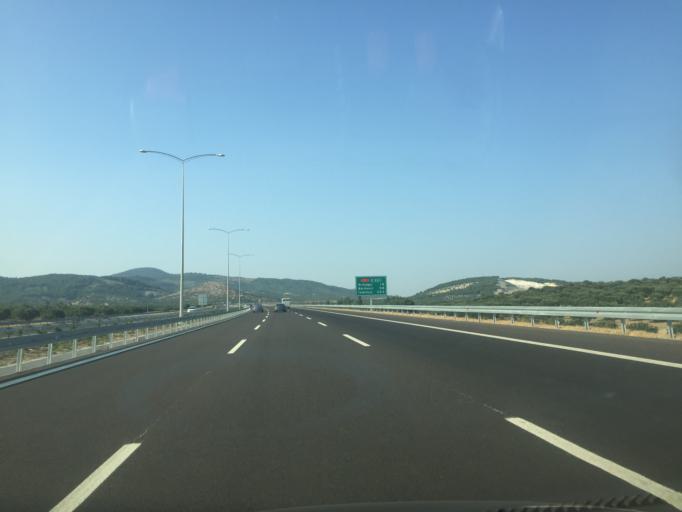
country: TR
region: Manisa
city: Zeytinliova
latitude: 38.9749
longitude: 27.7311
